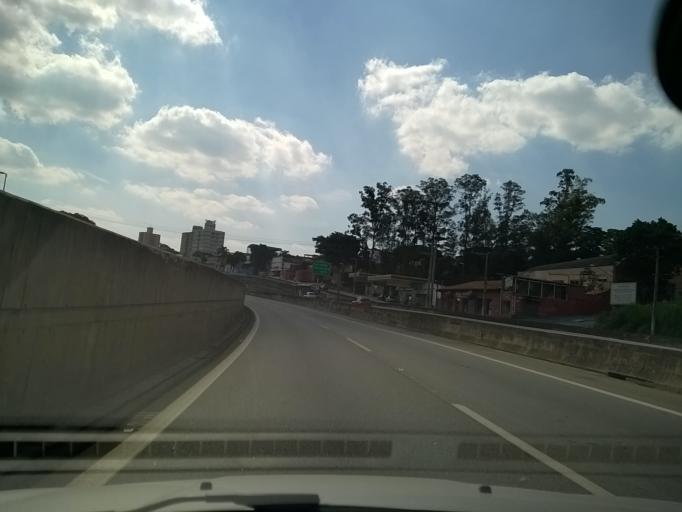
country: BR
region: Sao Paulo
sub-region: Osasco
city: Osasco
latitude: -23.5104
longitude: -46.7285
